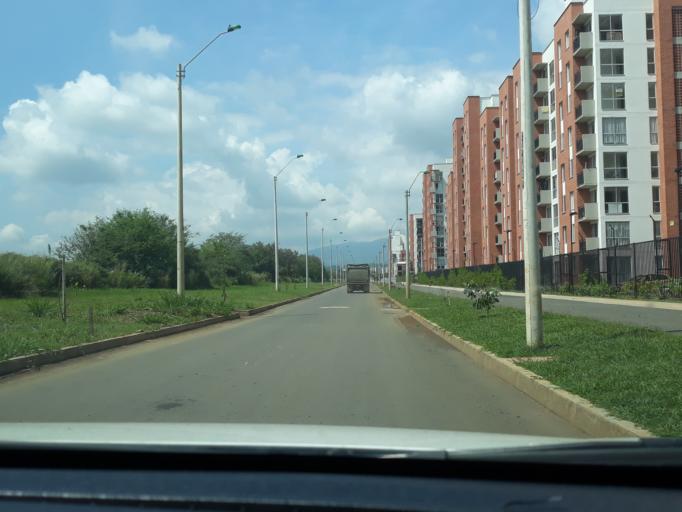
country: CO
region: Valle del Cauca
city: Cali
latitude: 3.3679
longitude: -76.5047
